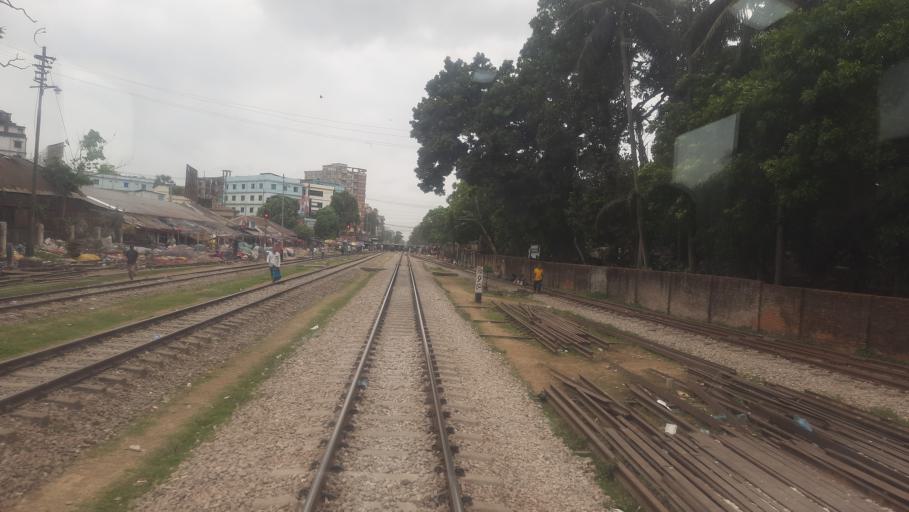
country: BD
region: Chittagong
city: Feni
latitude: 23.0145
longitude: 91.4019
